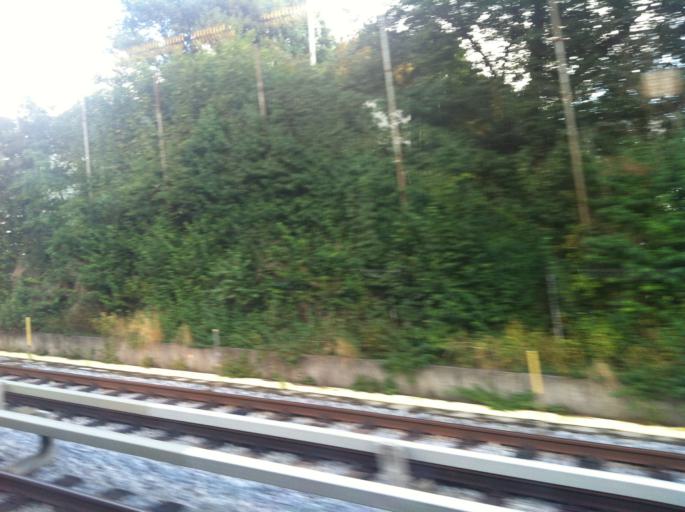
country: DE
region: Bavaria
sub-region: Upper Bavaria
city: Unterfoehring
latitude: 48.2071
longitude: 11.6146
